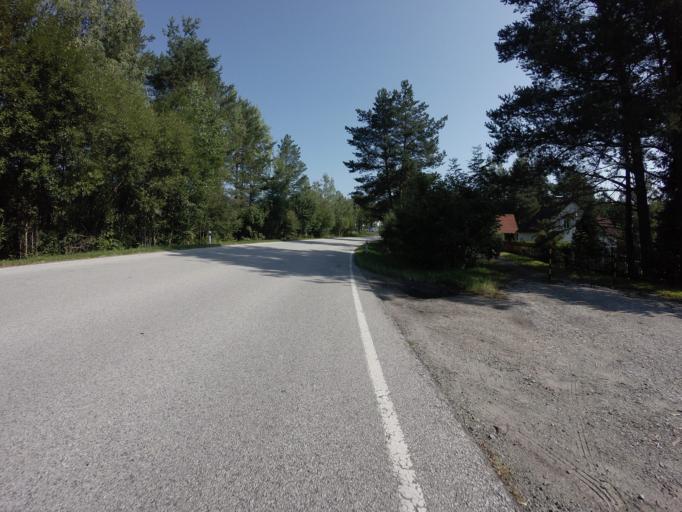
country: CZ
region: Jihocesky
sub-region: Okres Cesky Krumlov
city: Vyssi Brod
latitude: 48.5854
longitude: 14.3206
